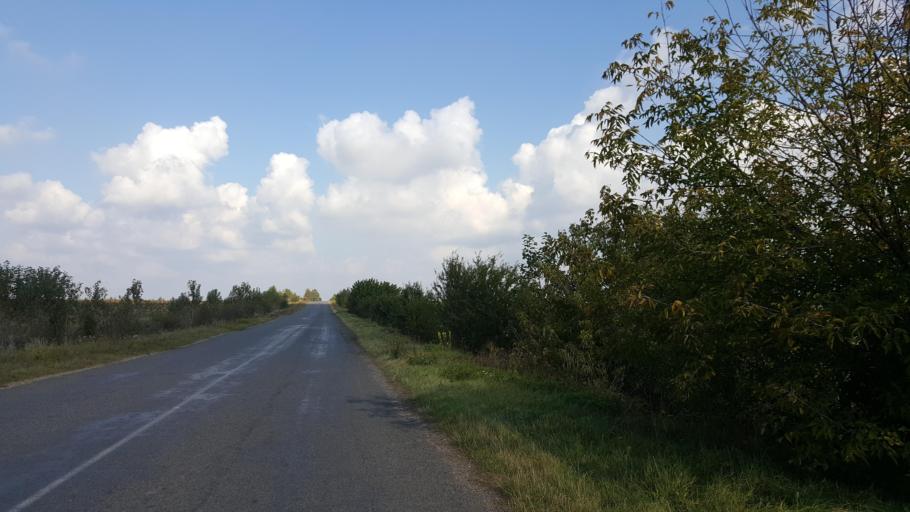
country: BY
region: Brest
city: Kamyanyets
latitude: 52.4157
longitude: 23.8029
